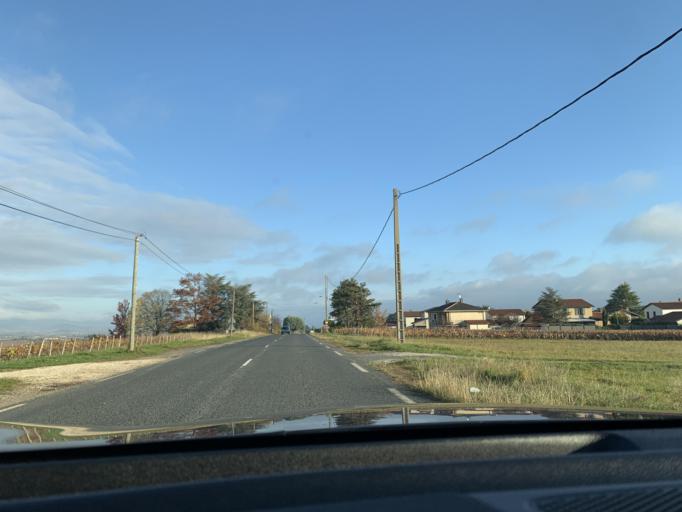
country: FR
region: Rhone-Alpes
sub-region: Departement du Rhone
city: Pommiers
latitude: 45.9478
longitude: 4.6911
